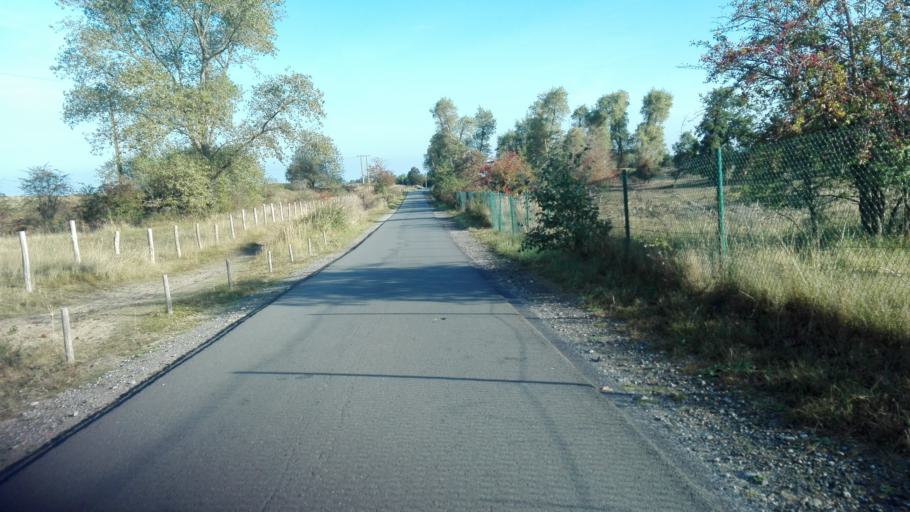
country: FR
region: Nord-Pas-de-Calais
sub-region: Departement du Nord
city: Ghyvelde
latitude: 51.0623
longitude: 2.5629
